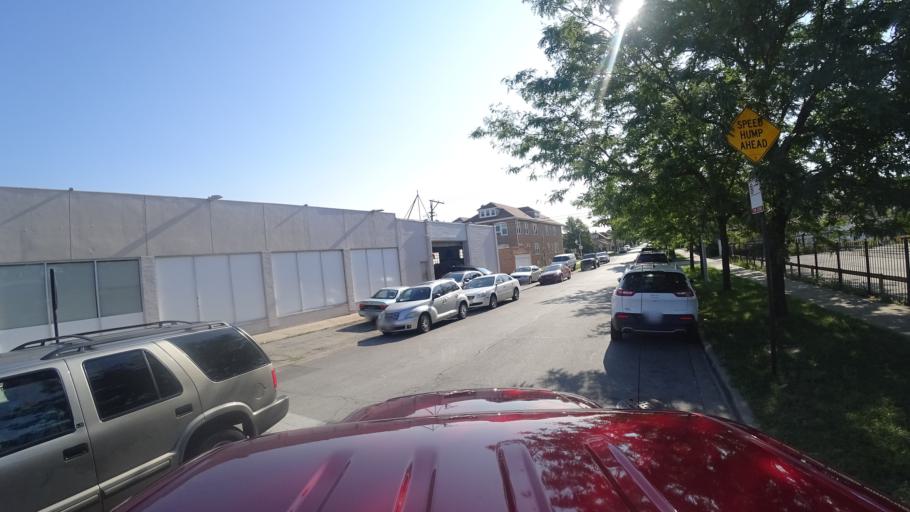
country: US
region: Illinois
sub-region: Cook County
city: Cicero
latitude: 41.8060
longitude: -87.7234
